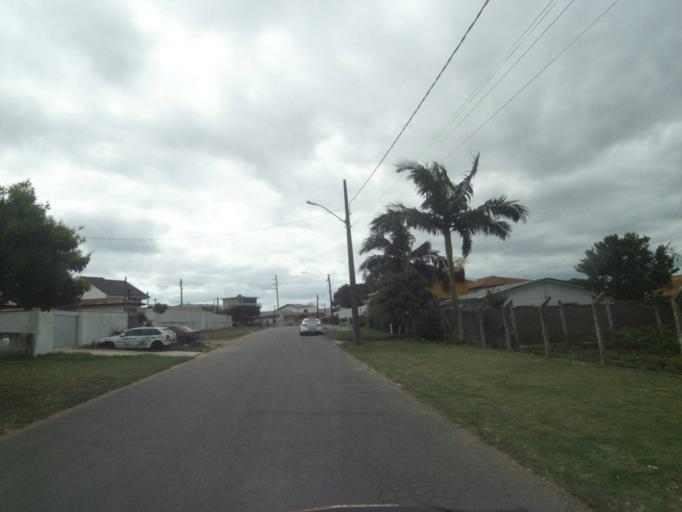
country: BR
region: Parana
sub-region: Sao Jose Dos Pinhais
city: Sao Jose dos Pinhais
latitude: -25.5553
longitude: -49.2547
